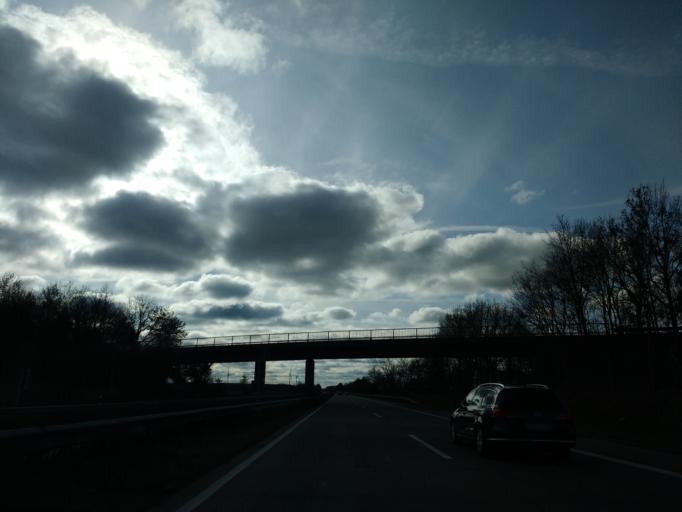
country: DE
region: Lower Saxony
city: Midlum
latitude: 53.6684
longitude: 8.6580
